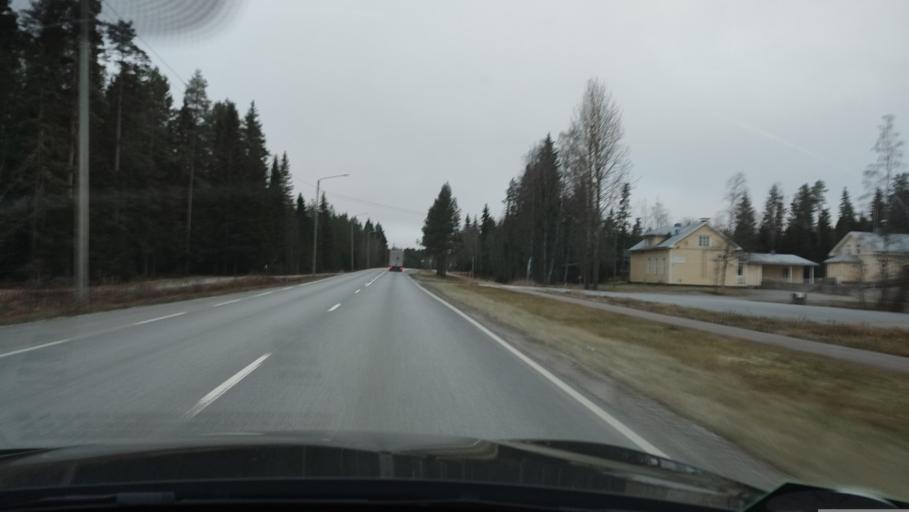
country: FI
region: Southern Ostrobothnia
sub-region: Suupohja
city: Kauhajoki
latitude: 62.3986
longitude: 22.1581
